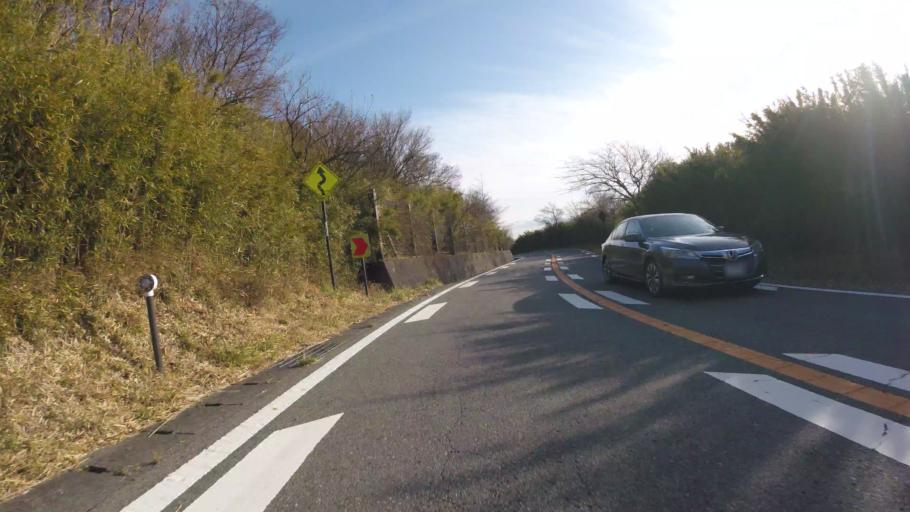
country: JP
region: Kanagawa
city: Yugawara
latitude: 35.1414
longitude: 139.0324
